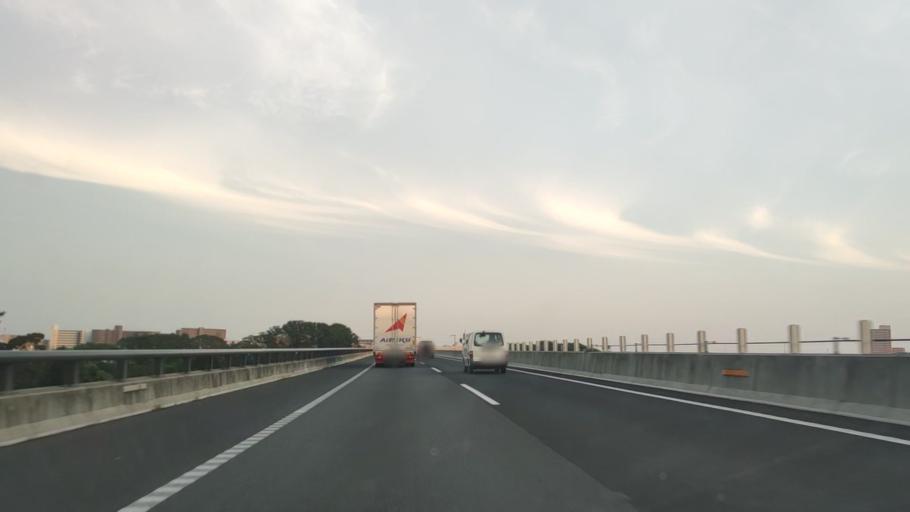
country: JP
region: Kanagawa
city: Atsugi
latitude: 35.4555
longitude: 139.3731
